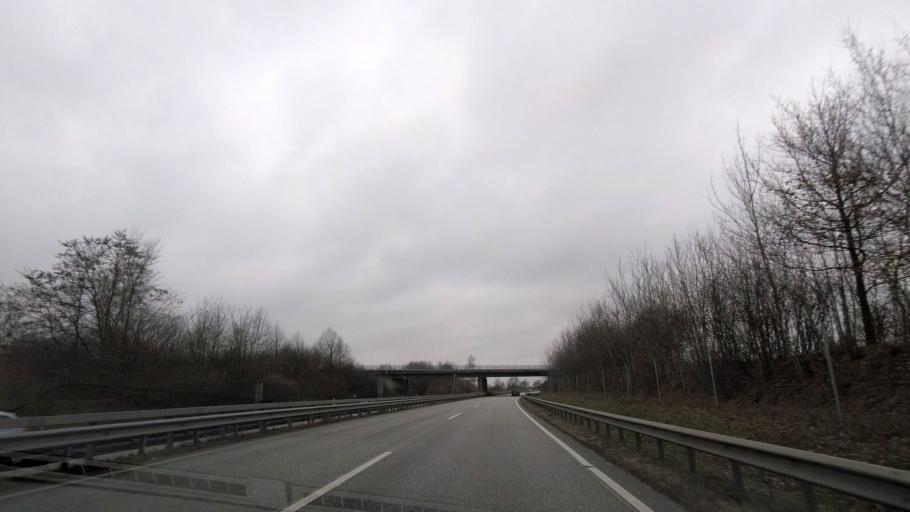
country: DE
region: Schleswig-Holstein
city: Negernbotel
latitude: 53.9729
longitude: 10.2404
